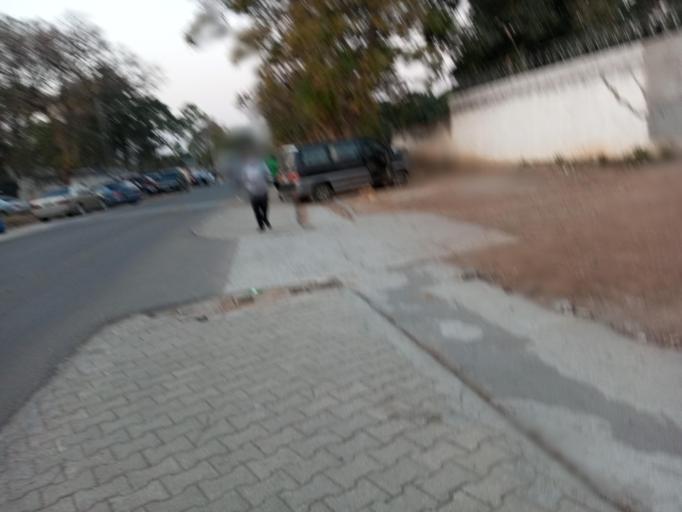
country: ZM
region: Lusaka
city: Lusaka
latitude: -15.4033
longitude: 28.2956
